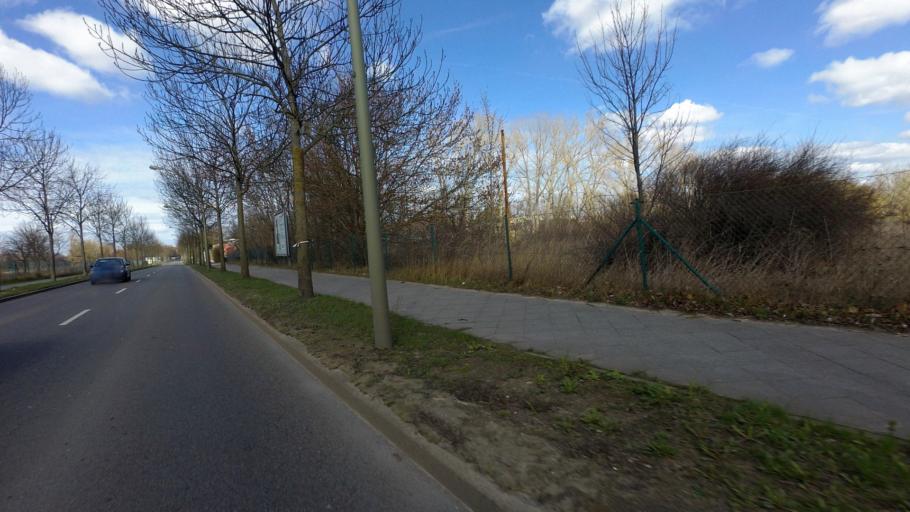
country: DE
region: Berlin
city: Blankenburg
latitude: 52.5862
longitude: 13.4585
